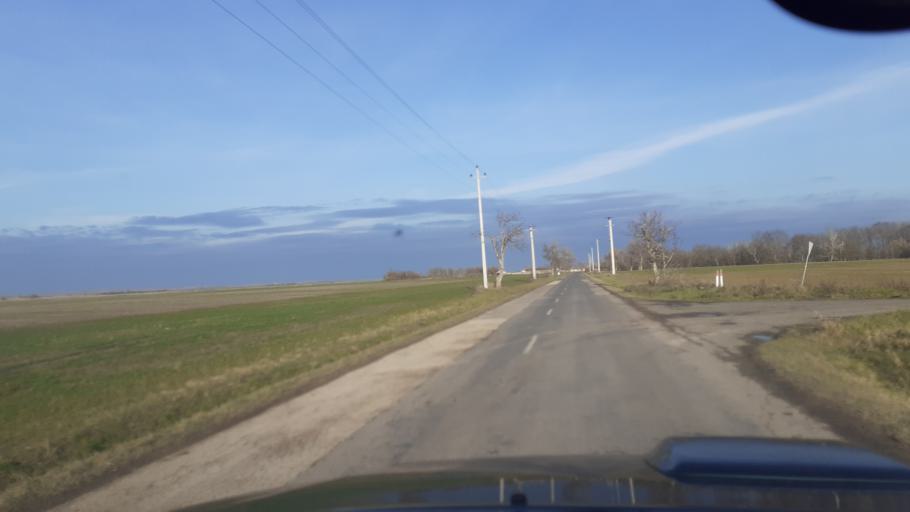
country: HU
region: Pest
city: Domsod
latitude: 47.1049
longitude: 19.0510
